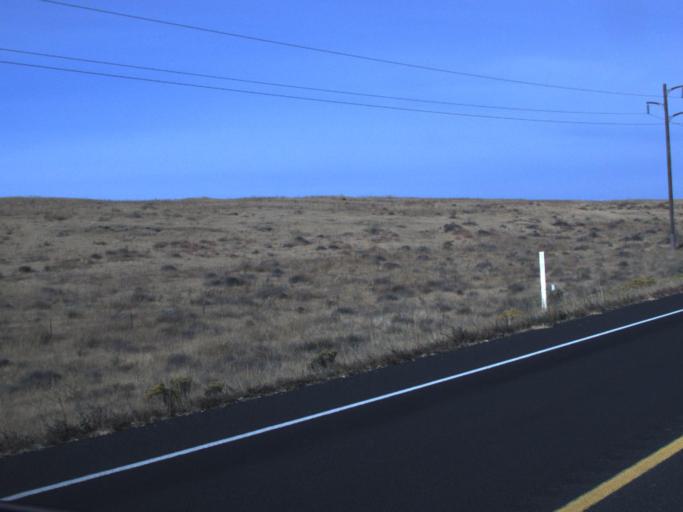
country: US
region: Oregon
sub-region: Morrow County
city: Boardman
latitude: 45.8892
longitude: -119.7042
